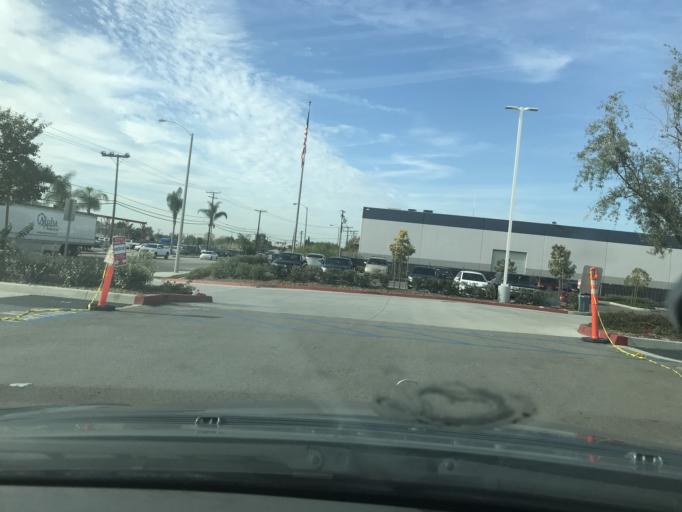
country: US
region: California
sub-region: Los Angeles County
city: Santa Fe Springs
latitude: 33.9320
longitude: -118.0700
